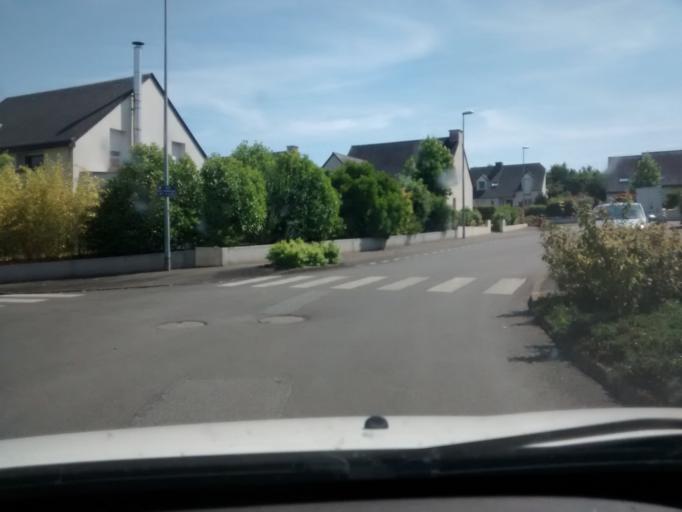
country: FR
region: Brittany
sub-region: Departement d'Ille-et-Vilaine
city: Chantepie
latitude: 48.1046
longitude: -1.6103
